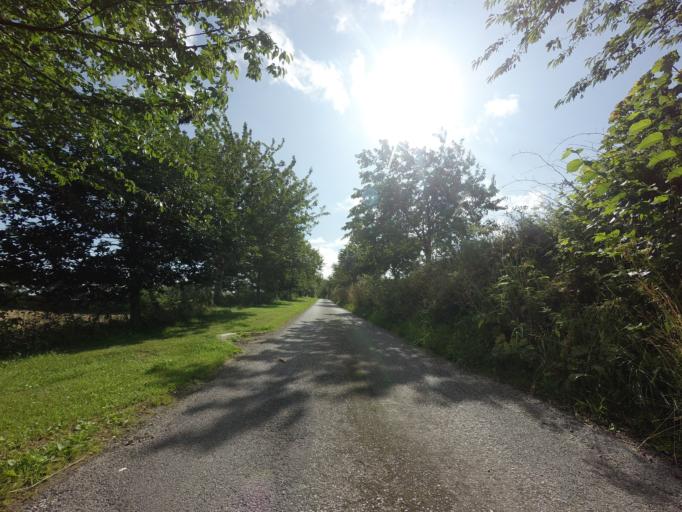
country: GB
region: Scotland
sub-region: Highland
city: Nairn
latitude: 57.5527
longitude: -3.8636
